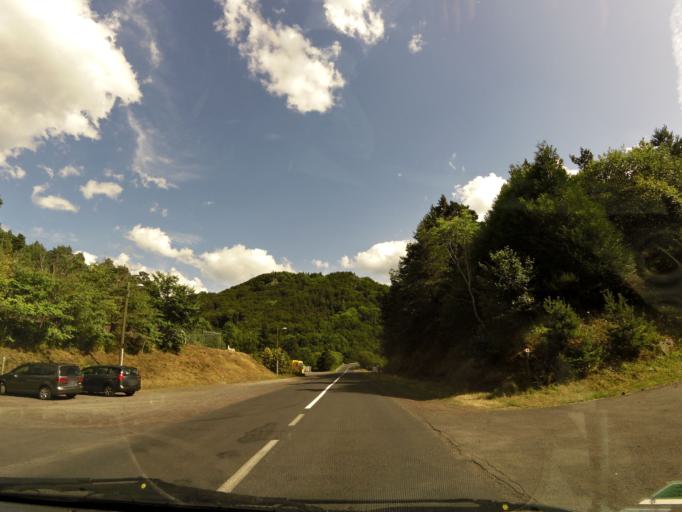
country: FR
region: Auvergne
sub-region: Departement du Puy-de-Dome
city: Aydat
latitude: 45.5694
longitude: 2.9466
